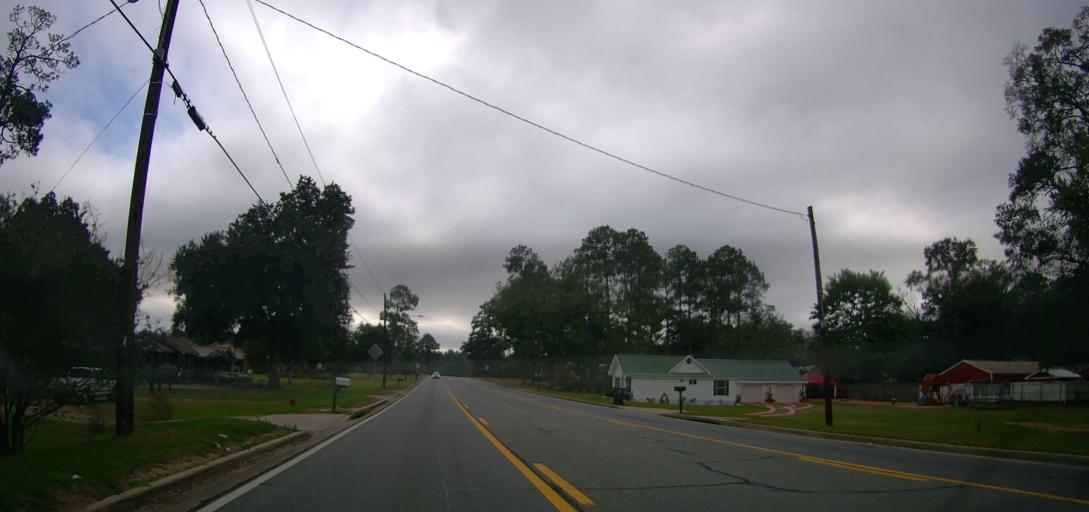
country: US
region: Georgia
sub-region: Tift County
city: Omega
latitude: 31.2679
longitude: -83.6876
